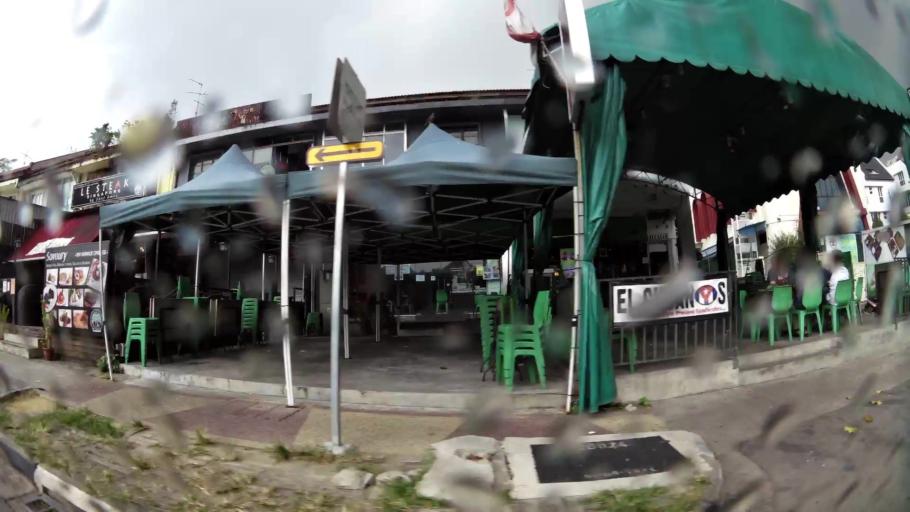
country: MY
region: Johor
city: Kampung Pasir Gudang Baru
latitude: 1.3977
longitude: 103.8732
